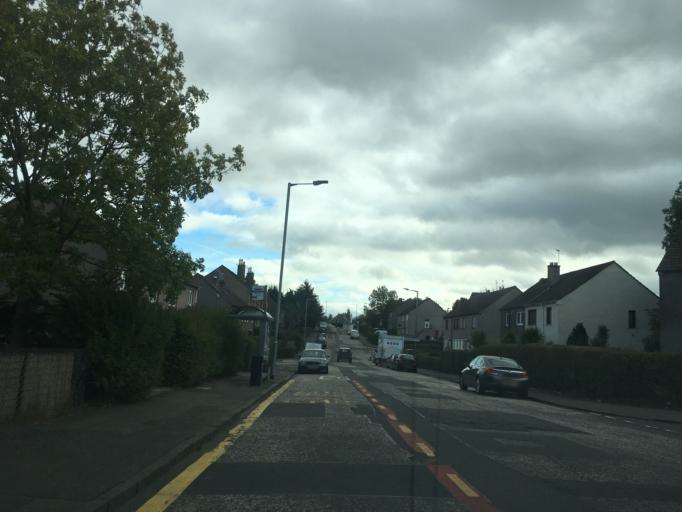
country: GB
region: Scotland
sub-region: Edinburgh
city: Edinburgh
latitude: 55.9627
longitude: -3.2482
